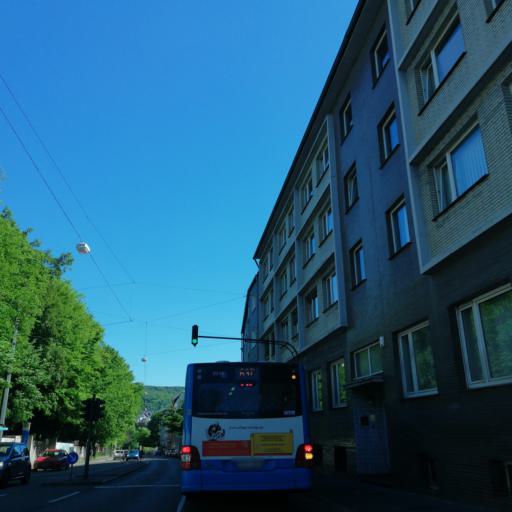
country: DE
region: North Rhine-Westphalia
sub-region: Regierungsbezirk Dusseldorf
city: Wuppertal
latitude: 51.2755
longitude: 7.1908
